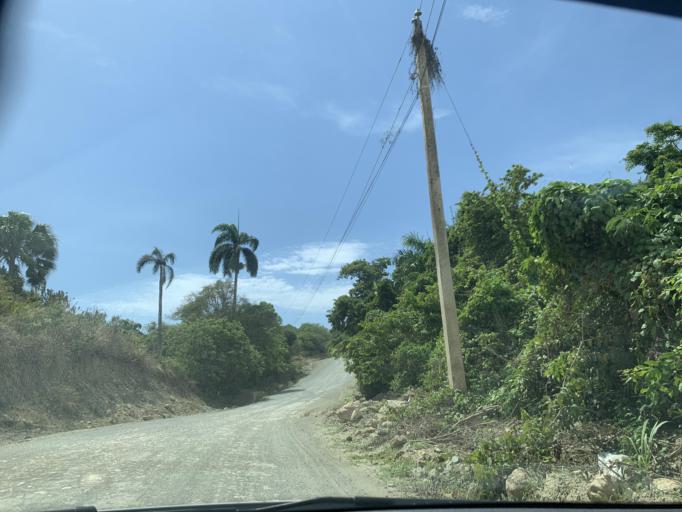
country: DO
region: Puerto Plata
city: Imbert
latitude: 19.8651
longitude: -70.8118
